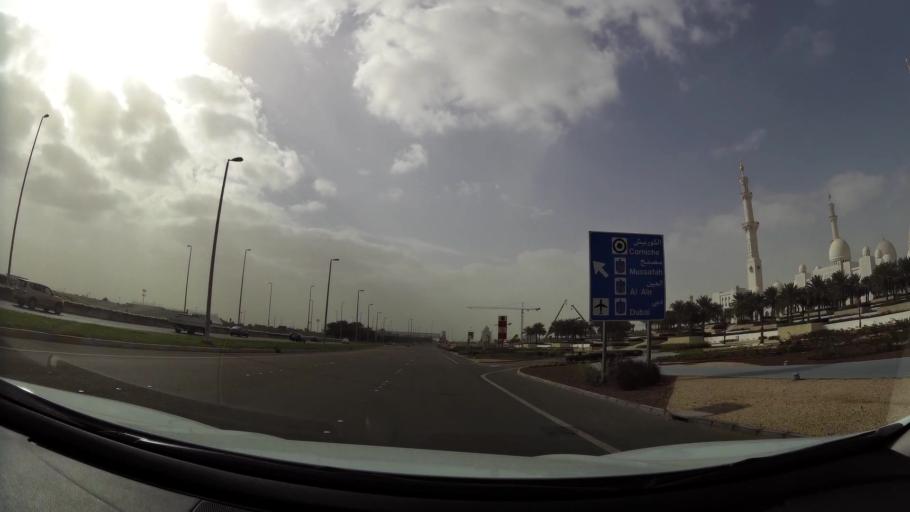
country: AE
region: Abu Dhabi
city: Abu Dhabi
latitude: 24.4139
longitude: 54.4779
